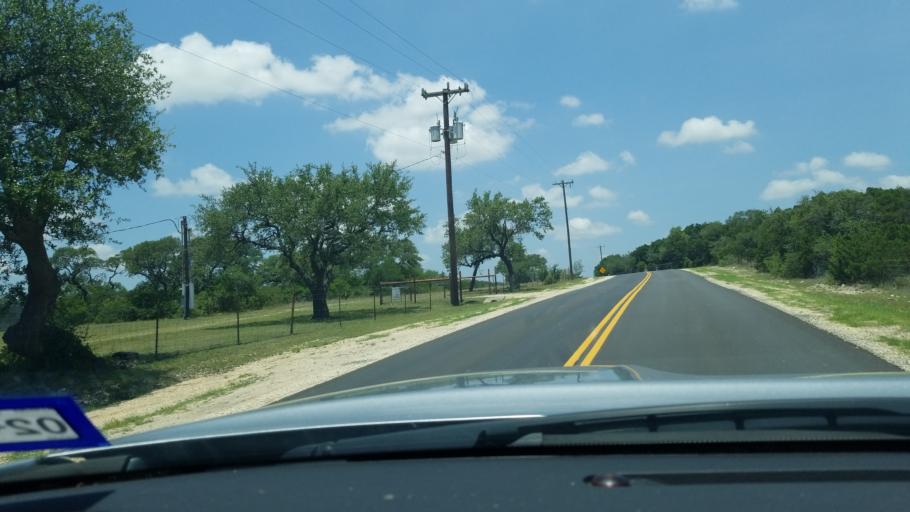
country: US
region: Texas
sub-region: Bexar County
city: Timberwood Park
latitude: 29.7017
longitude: -98.4547
